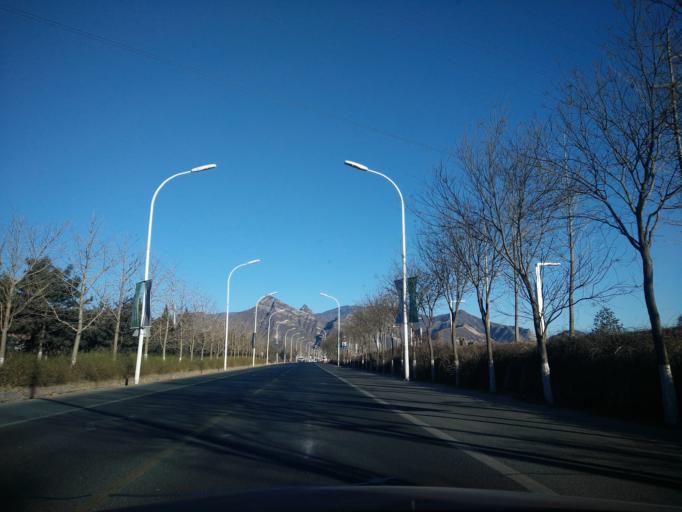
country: CN
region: Beijing
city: Junzhuang
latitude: 39.9772
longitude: 116.0843
